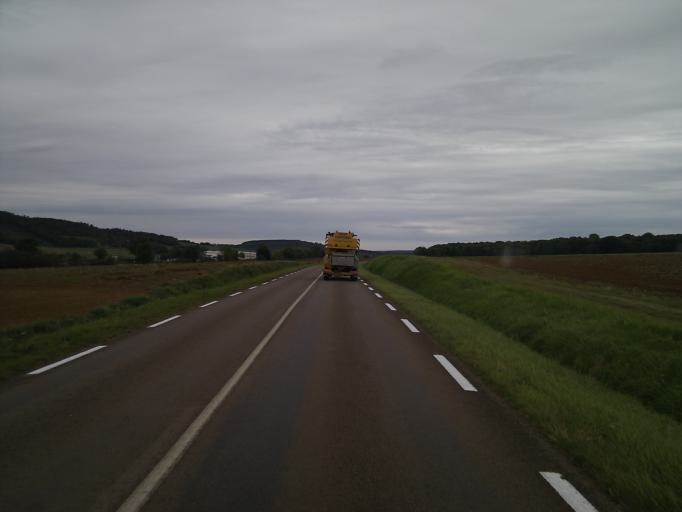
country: FR
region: Champagne-Ardenne
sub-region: Departement de la Haute-Marne
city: Chateauvillain
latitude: 48.0656
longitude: 4.9486
